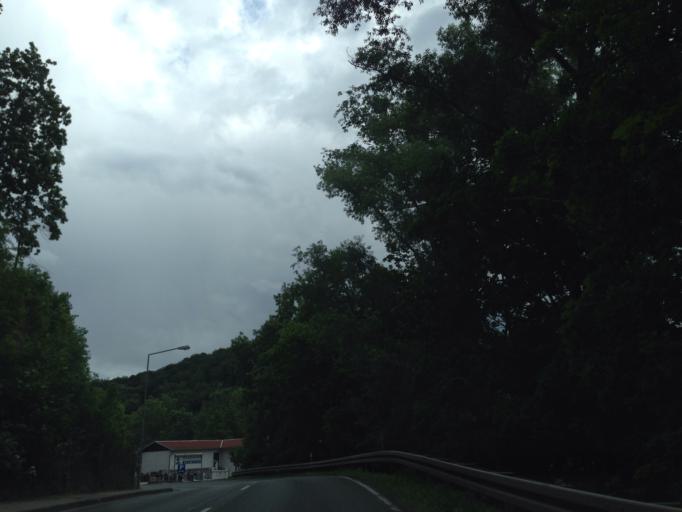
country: DE
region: Thuringia
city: Rudolstadt
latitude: 50.7311
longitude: 11.3338
